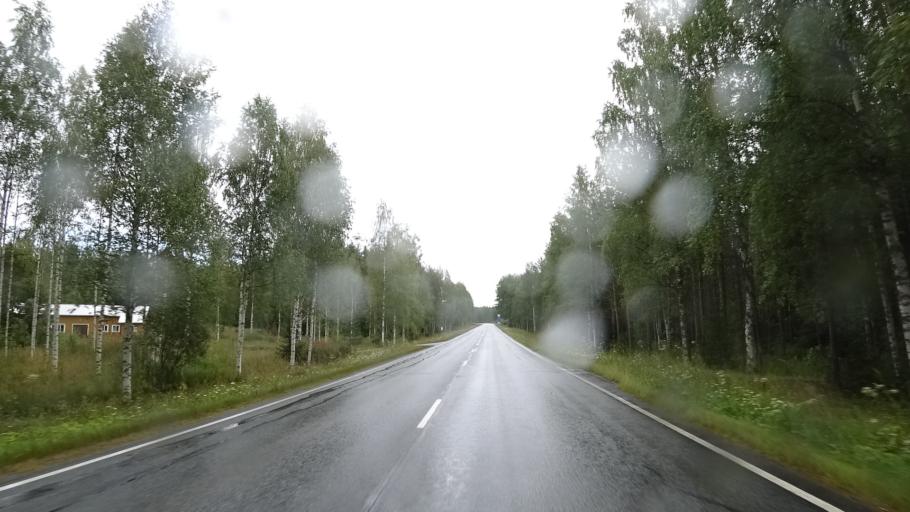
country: FI
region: North Karelia
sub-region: Keski-Karjala
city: Raeaekkylae
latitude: 62.0530
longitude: 29.6052
